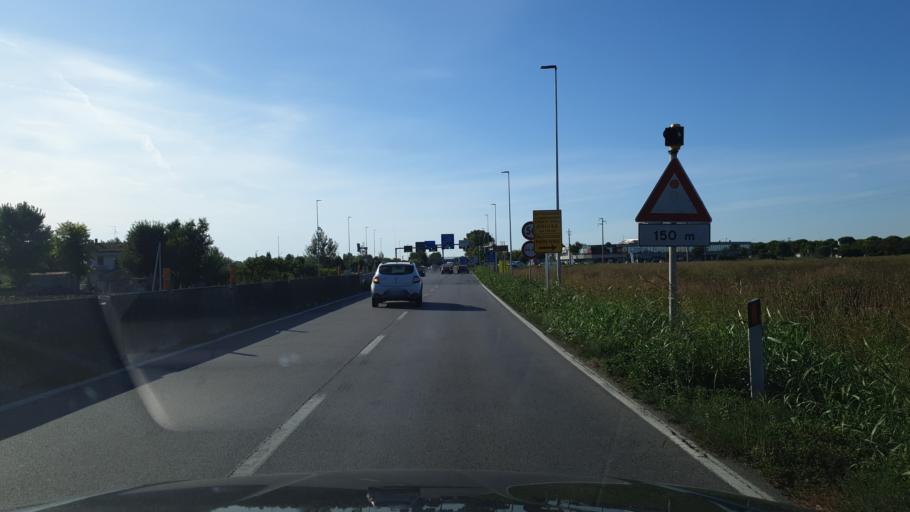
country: IT
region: Emilia-Romagna
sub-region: Provincia di Ravenna
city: Madonna Dell'Albero
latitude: 44.3773
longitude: 12.2169
